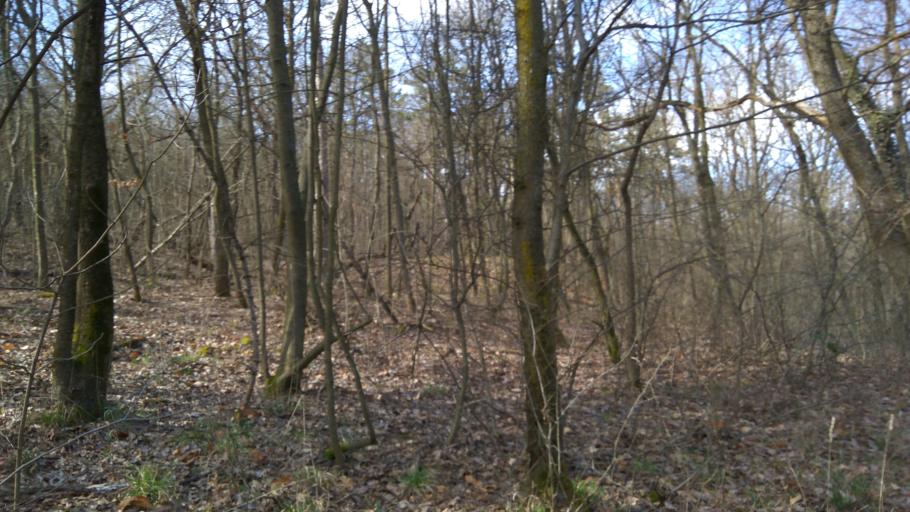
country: HU
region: Pest
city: Urom
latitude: 47.6146
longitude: 19.0116
